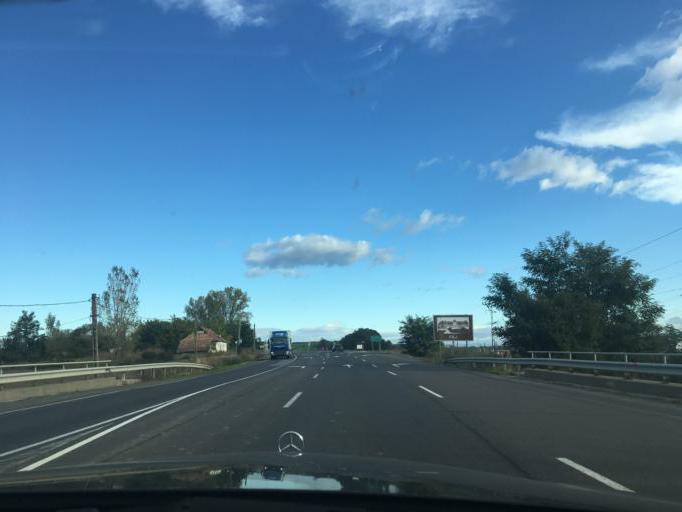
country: HU
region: Borsod-Abauj-Zemplen
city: Encs
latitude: 48.3617
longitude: 21.1393
